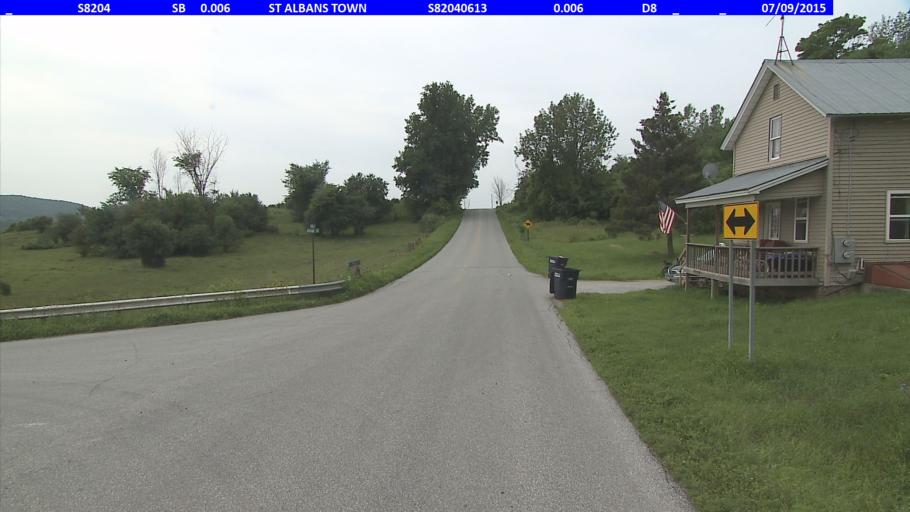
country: US
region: Vermont
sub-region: Franklin County
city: Saint Albans
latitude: 44.8030
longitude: -73.1133
